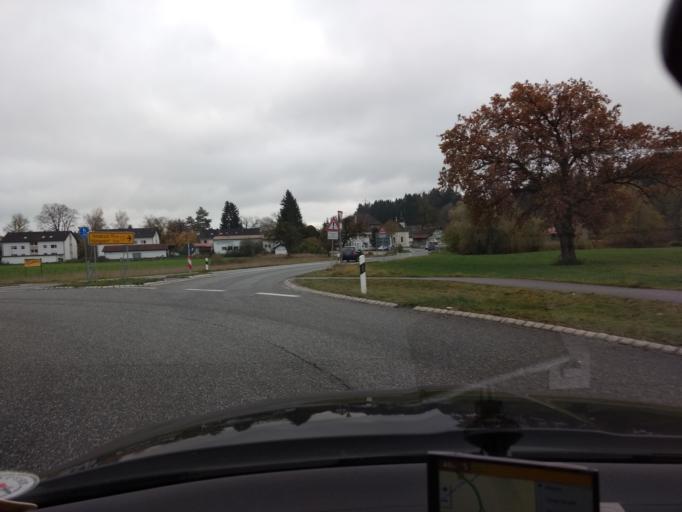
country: DE
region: Bavaria
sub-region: Upper Bavaria
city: Geretsried
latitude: 47.8623
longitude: 11.4684
